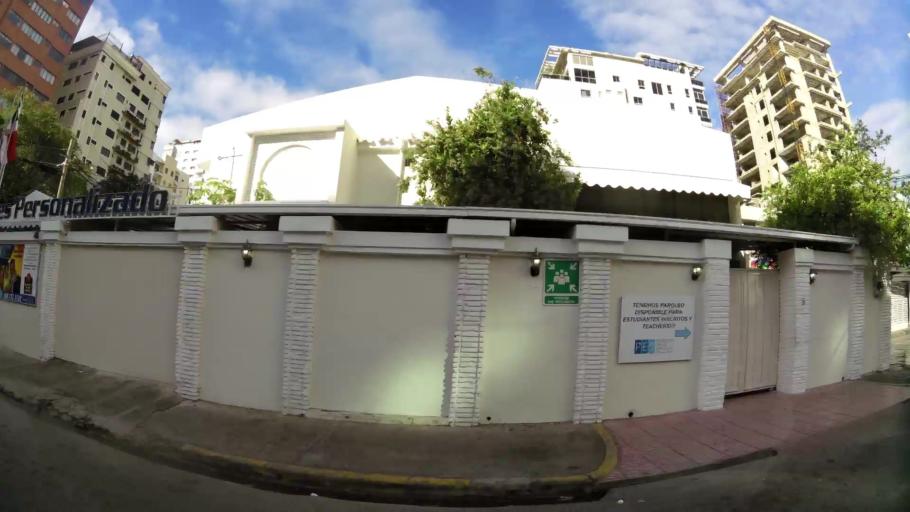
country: DO
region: Nacional
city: La Julia
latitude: 18.4777
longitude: -69.9397
